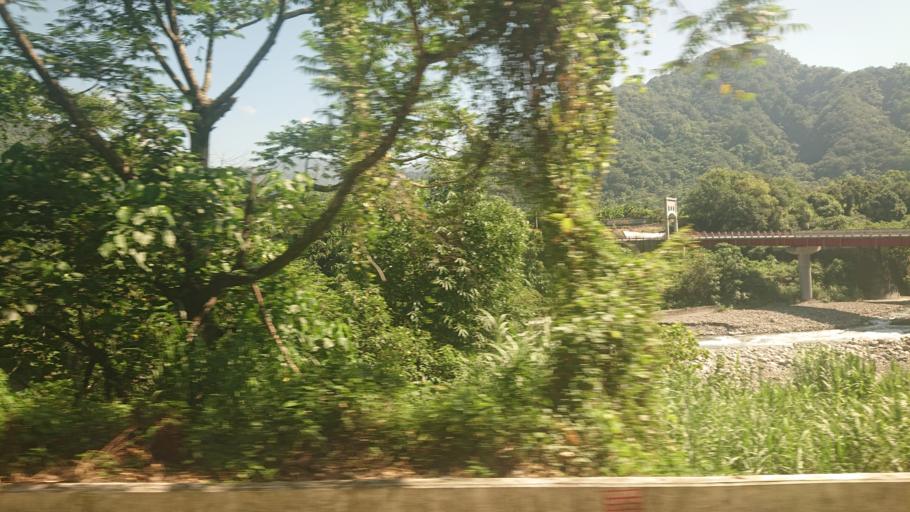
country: TW
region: Taiwan
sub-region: Nantou
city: Puli
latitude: 24.0624
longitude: 120.9528
